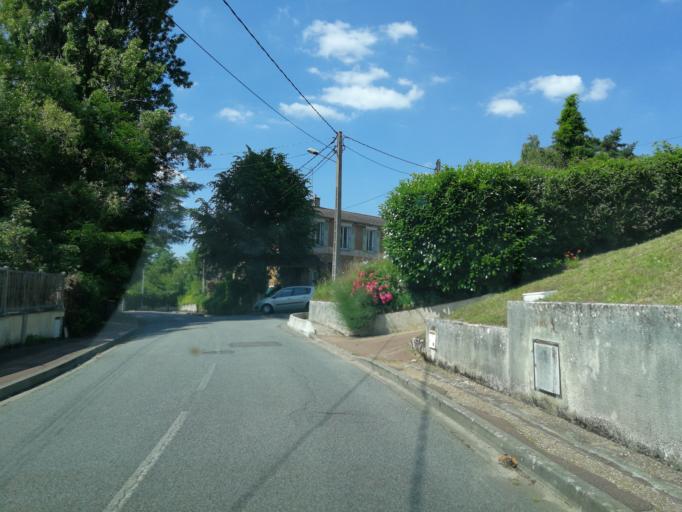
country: FR
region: Ile-de-France
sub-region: Departement des Yvelines
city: Saint-Remy-les-Chevreuse
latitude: 48.7120
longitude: 2.0695
